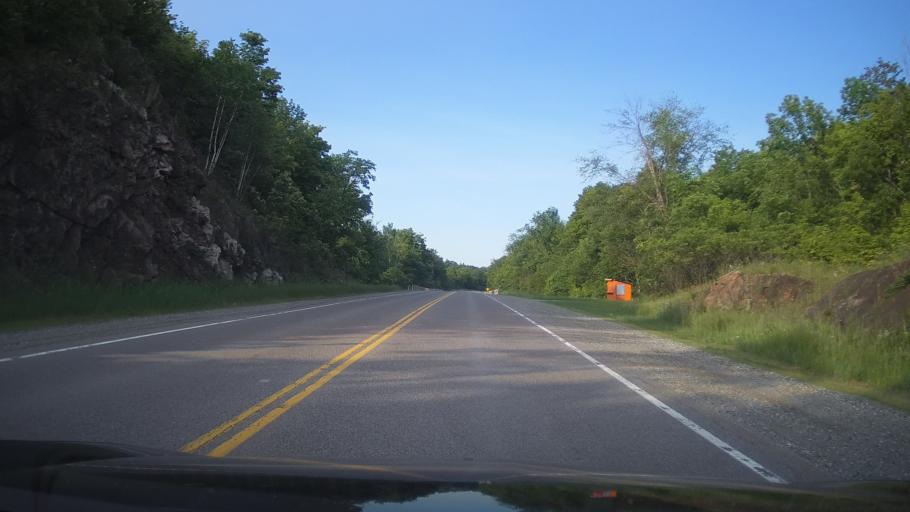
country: CA
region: Ontario
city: Perth
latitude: 44.7921
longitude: -76.7029
